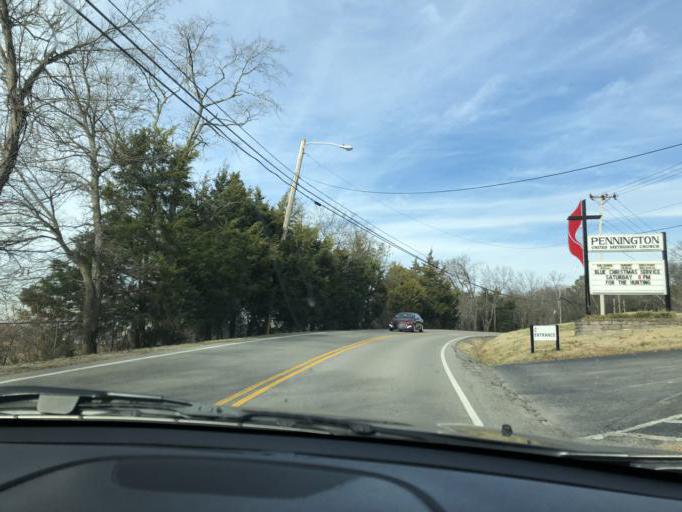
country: US
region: Tennessee
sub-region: Davidson County
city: Lakewood
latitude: 36.2187
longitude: -86.6896
